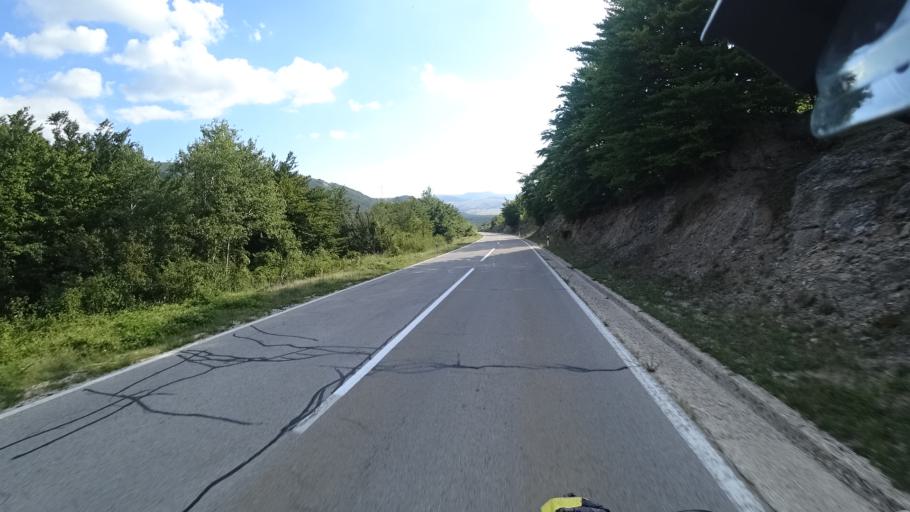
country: HR
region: Zadarska
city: Gracac
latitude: 44.2955
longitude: 16.0864
